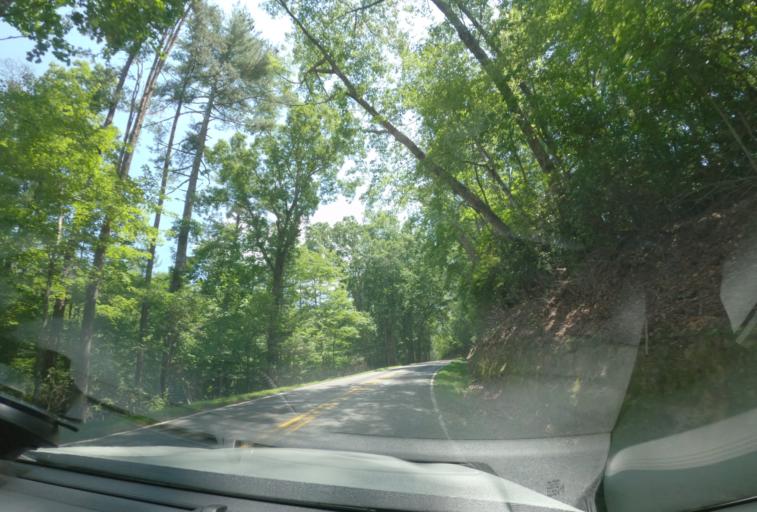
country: US
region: South Carolina
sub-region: Pickens County
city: Pickens
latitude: 34.9688
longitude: -82.8645
